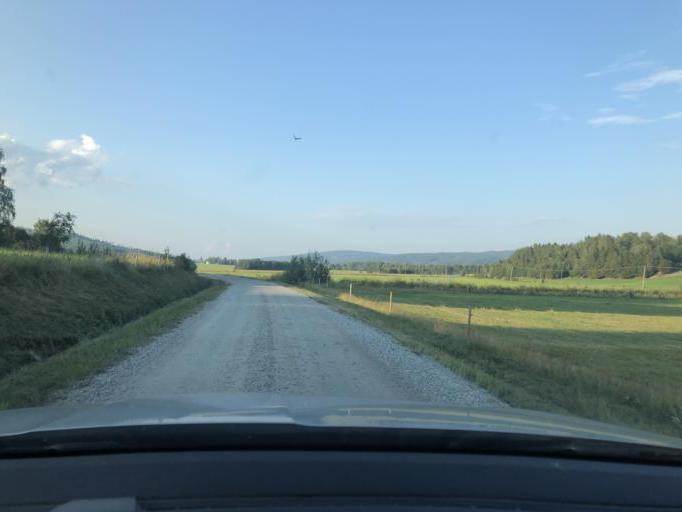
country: SE
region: Vaesternorrland
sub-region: Kramfors Kommun
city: Bollstabruk
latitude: 63.0650
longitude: 17.7346
